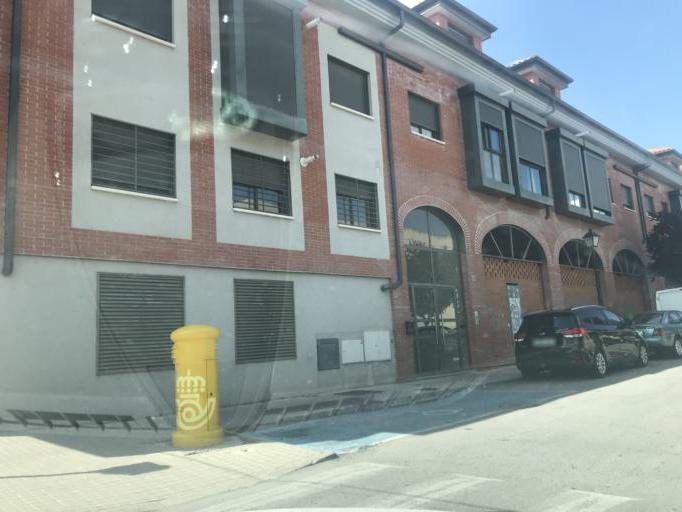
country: ES
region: Madrid
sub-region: Provincia de Madrid
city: Ajalvir
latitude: 40.5349
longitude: -3.4798
